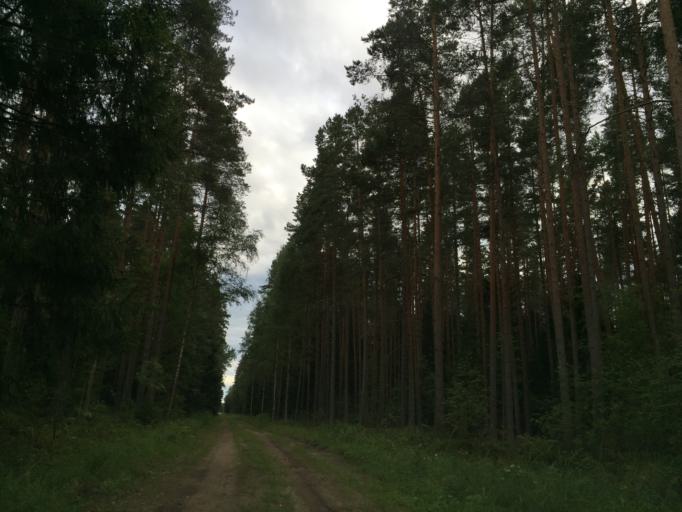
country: LV
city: Tireli
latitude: 56.8434
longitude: 23.6853
